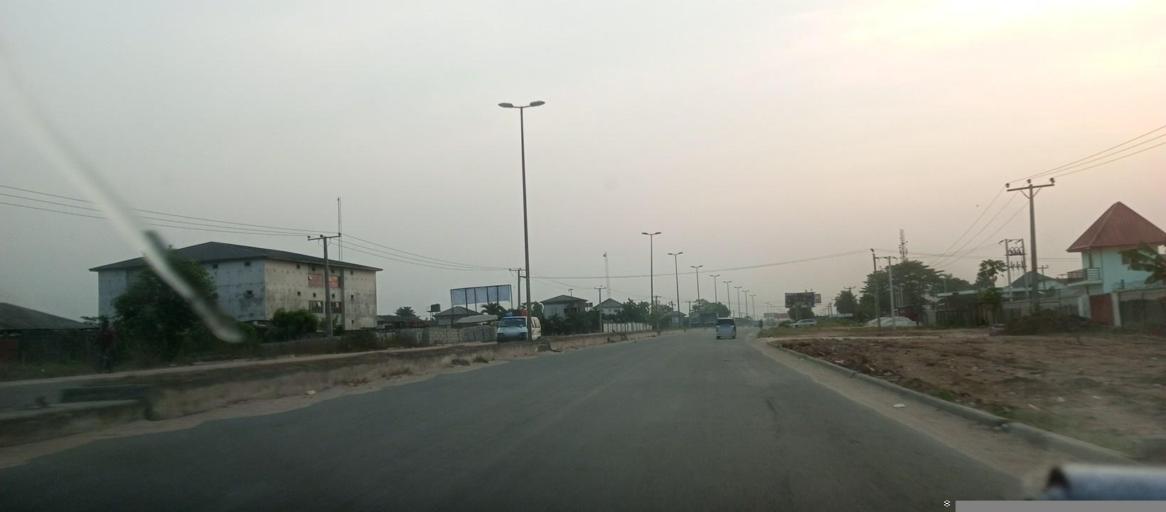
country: NG
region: Rivers
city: Emuoha
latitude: 4.9350
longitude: 7.0052
